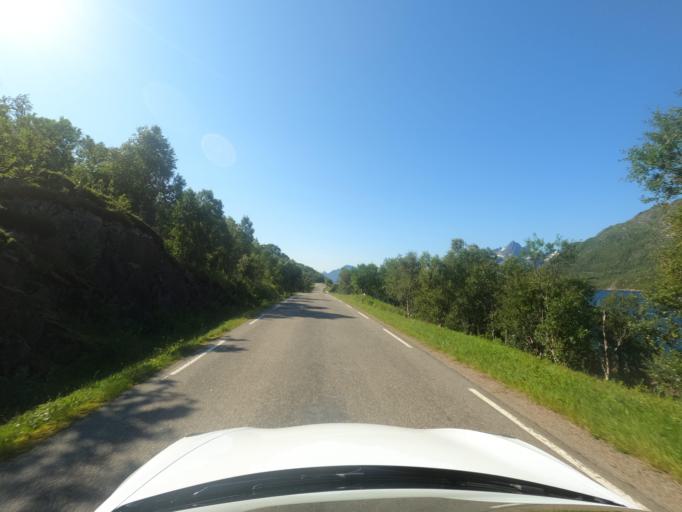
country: NO
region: Nordland
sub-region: Hadsel
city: Stokmarknes
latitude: 68.3800
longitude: 15.0869
